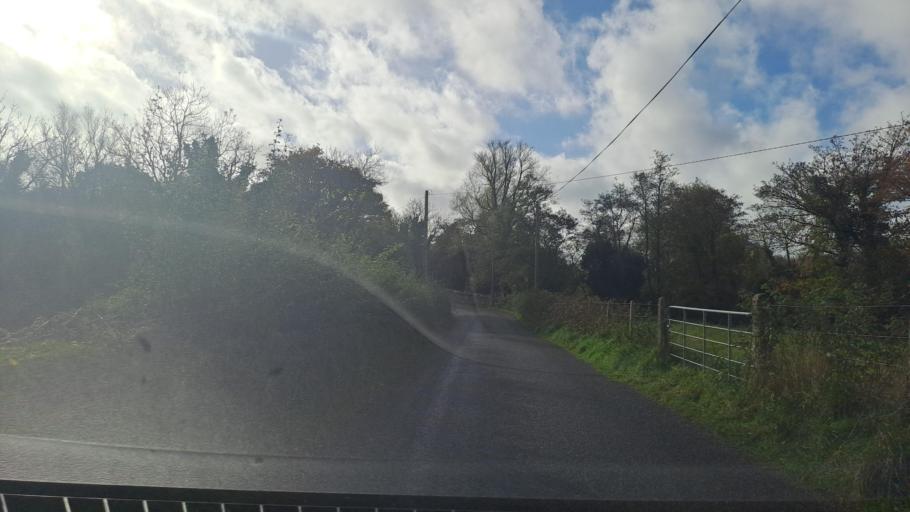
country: IE
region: Ulster
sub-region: An Cabhan
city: Cootehill
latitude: 54.0389
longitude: -6.9962
